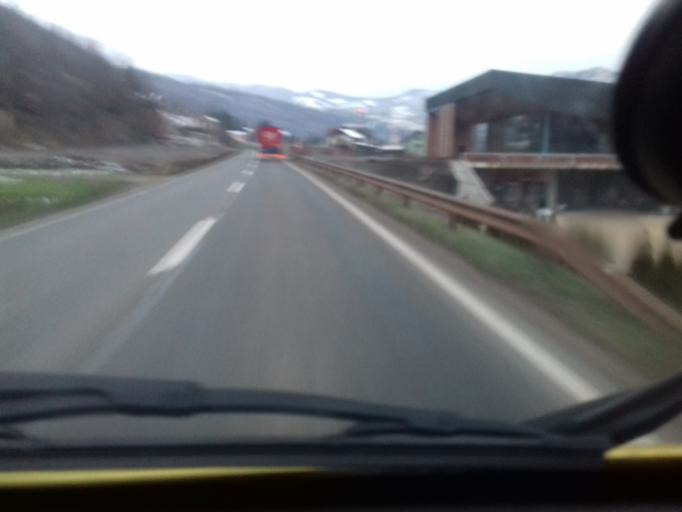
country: BA
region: Federation of Bosnia and Herzegovina
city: Zeljezno Polje
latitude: 44.3754
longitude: 17.9976
